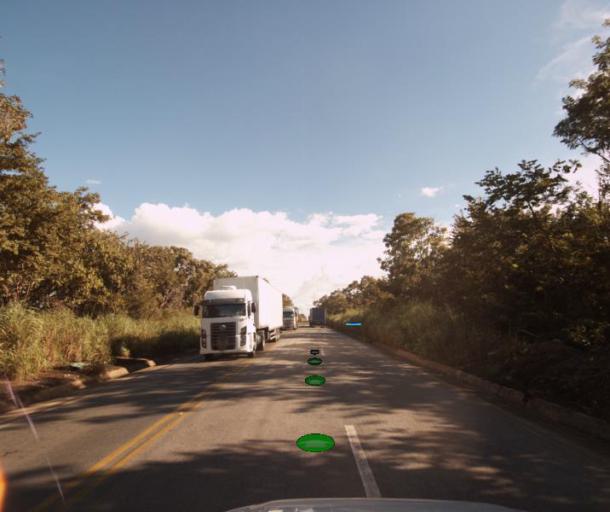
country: BR
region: Goias
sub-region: Porangatu
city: Porangatu
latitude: -13.0950
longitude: -49.1957
